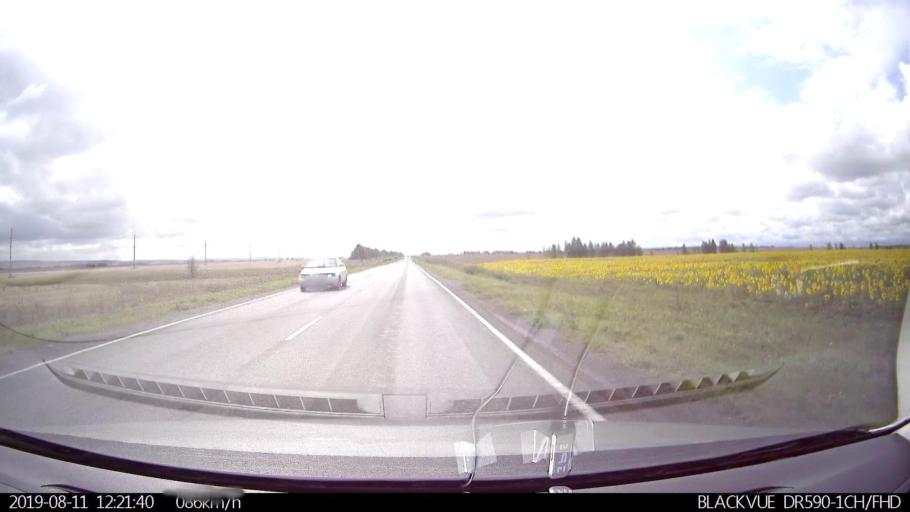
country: RU
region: Ulyanovsk
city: Ignatovka
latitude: 53.9181
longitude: 47.9571
